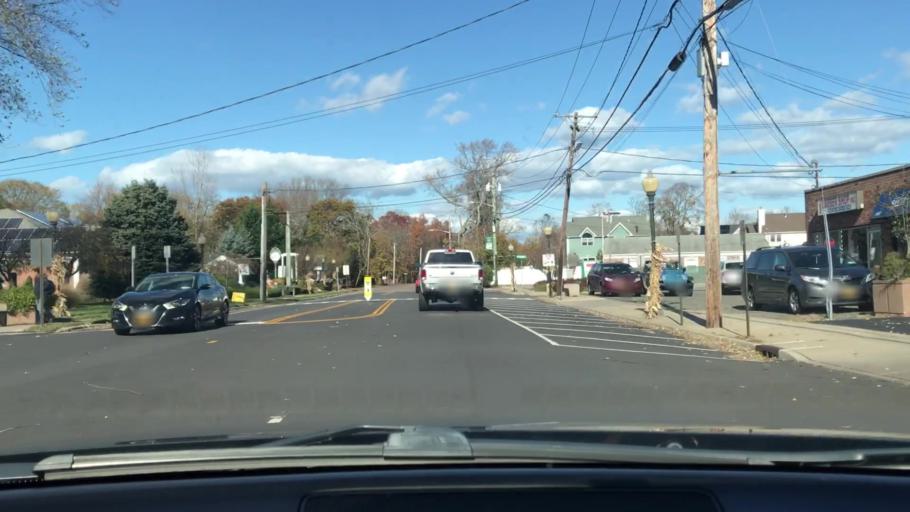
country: US
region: New York
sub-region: Suffolk County
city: Lake Grove
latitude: 40.8526
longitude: -73.1149
